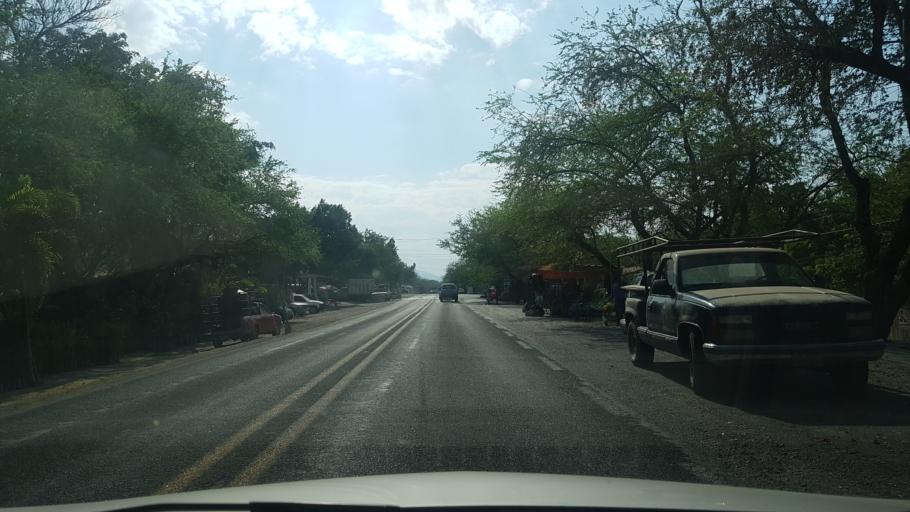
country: MX
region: Morelos
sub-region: Amacuzac
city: San Gabriel las Palmas
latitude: 18.6118
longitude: -99.3483
